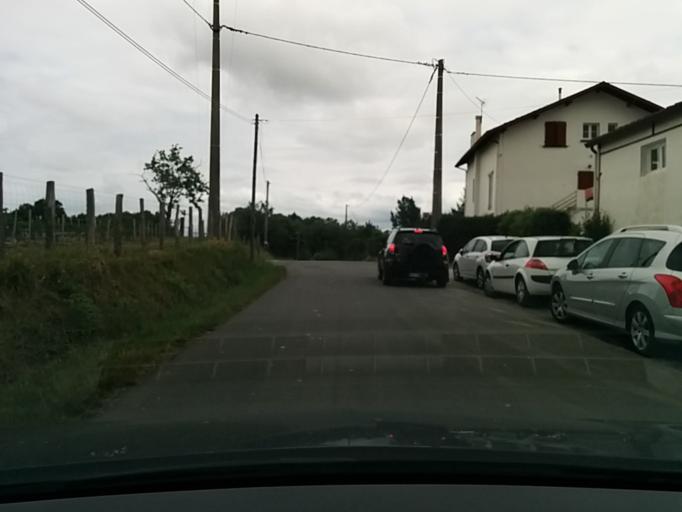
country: FR
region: Aquitaine
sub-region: Departement des Pyrenees-Atlantiques
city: Espelette
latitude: 43.3464
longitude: -1.4388
